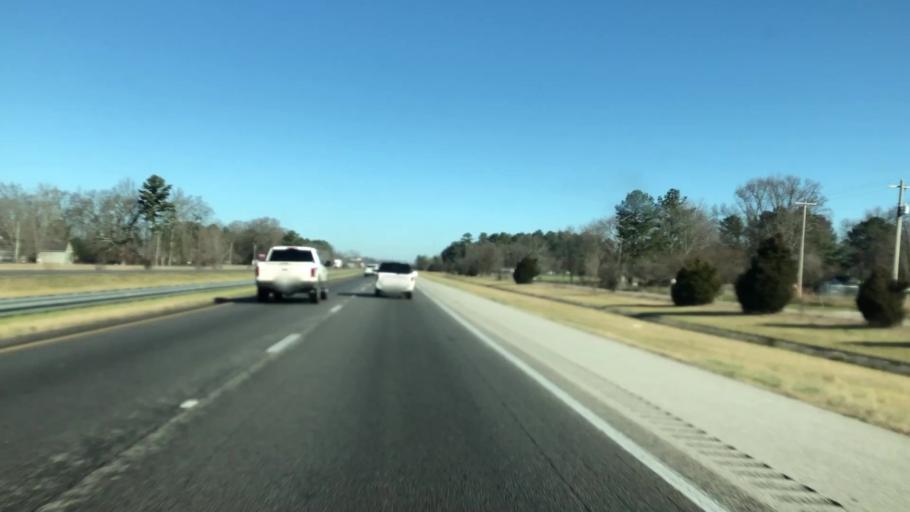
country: US
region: Alabama
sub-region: Limestone County
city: Athens
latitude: 34.8648
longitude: -86.9248
